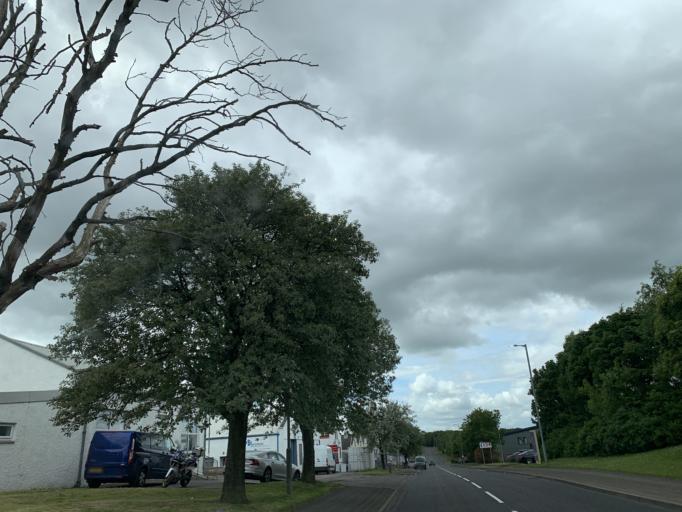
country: GB
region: Scotland
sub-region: Renfrewshire
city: Renfrew
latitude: 55.8568
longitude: -4.3704
